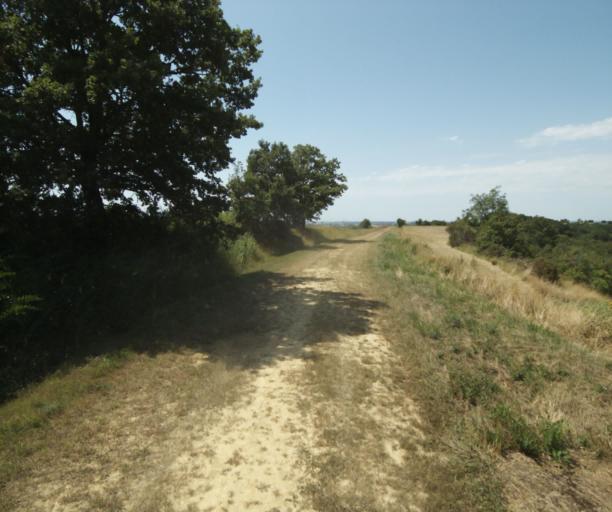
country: FR
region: Midi-Pyrenees
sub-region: Departement de la Haute-Garonne
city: Saint-Felix-Lauragais
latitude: 43.4411
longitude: 1.8710
